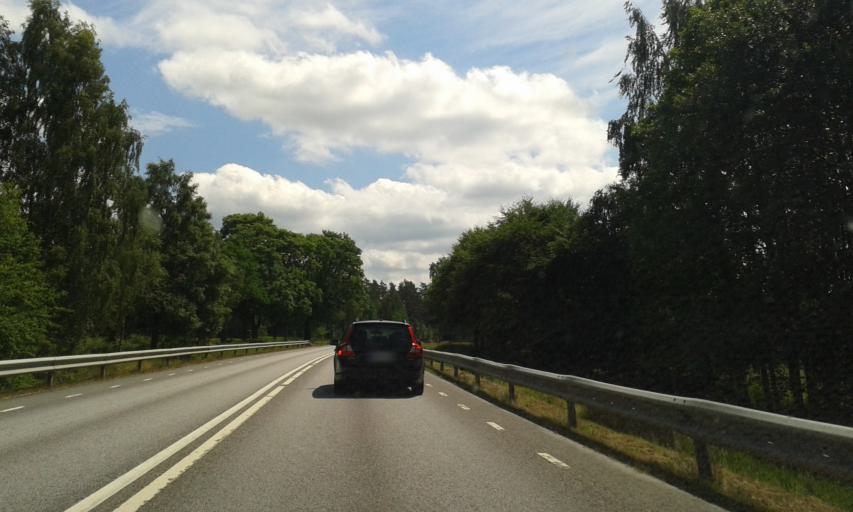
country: SE
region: Joenkoeping
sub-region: Varnamo Kommun
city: Rydaholm
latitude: 56.9703
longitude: 14.3302
